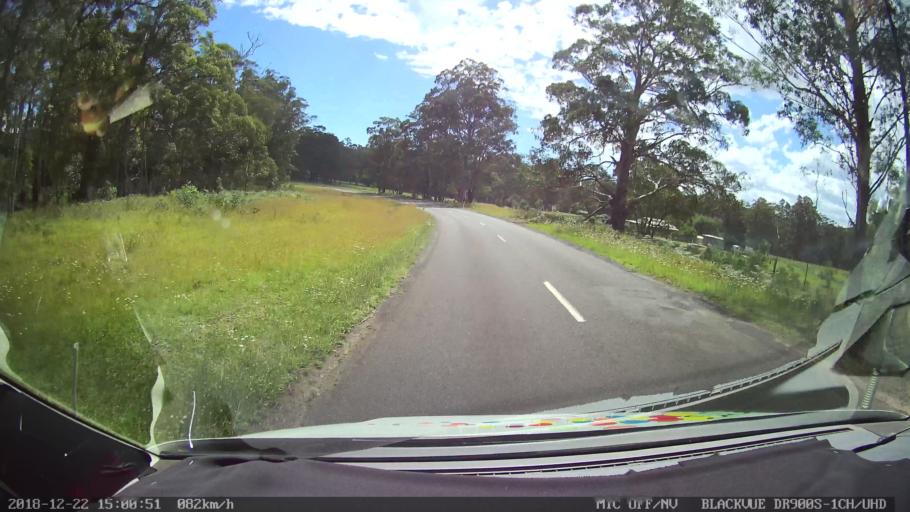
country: AU
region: New South Wales
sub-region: Bellingen
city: Dorrigo
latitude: -30.2496
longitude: 152.4645
